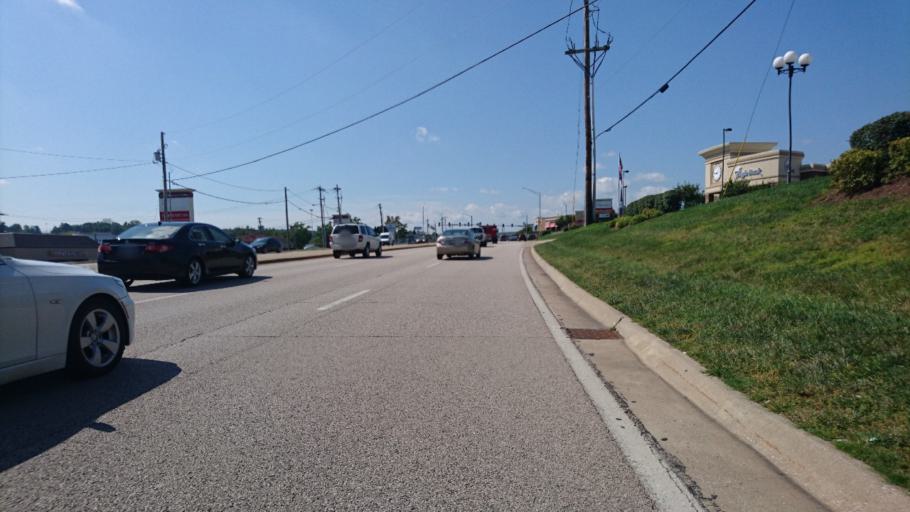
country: US
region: Missouri
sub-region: Saint Louis County
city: Manchester
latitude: 38.5928
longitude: -90.5027
